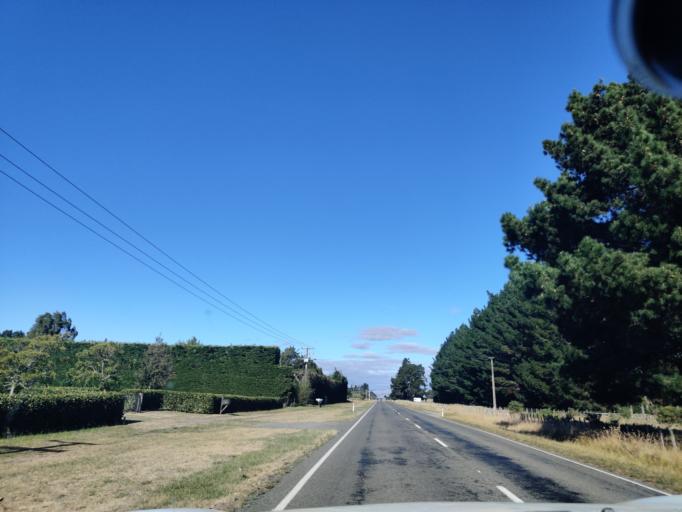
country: NZ
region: Manawatu-Wanganui
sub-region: Horowhenua District
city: Foxton
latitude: -40.3976
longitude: 175.3448
